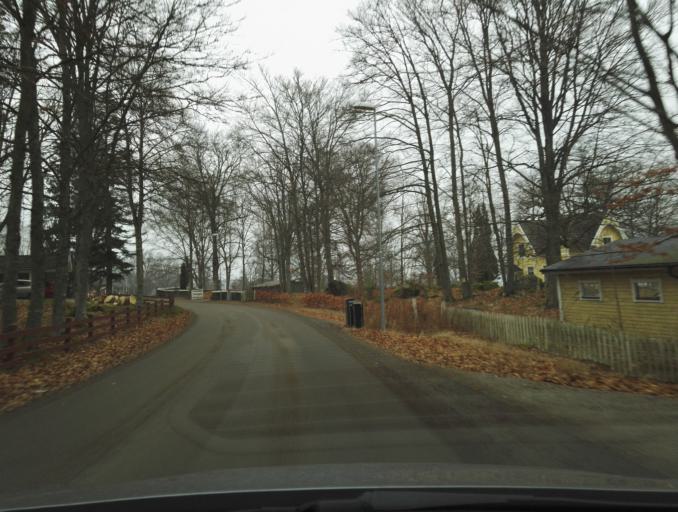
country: SE
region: Kronoberg
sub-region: Vaxjo Kommun
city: Vaexjoe
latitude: 56.9254
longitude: 14.8174
